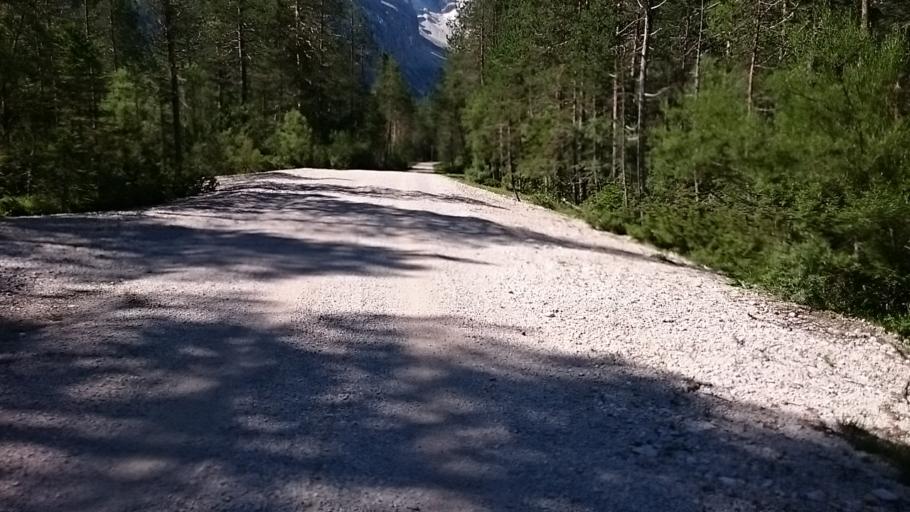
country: IT
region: Trentino-Alto Adige
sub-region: Bolzano
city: Dobbiaco
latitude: 46.6207
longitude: 12.2230
